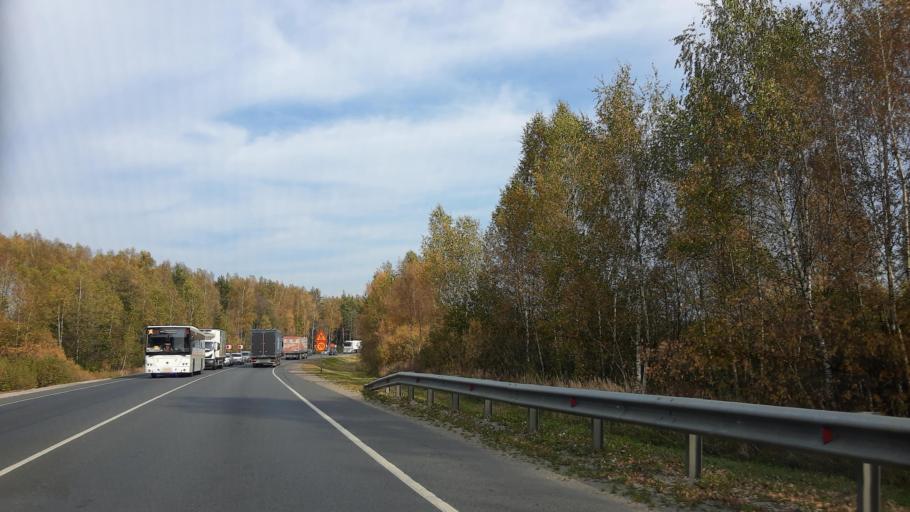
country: RU
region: Moskovskaya
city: Fryazevo
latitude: 55.7318
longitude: 38.4290
